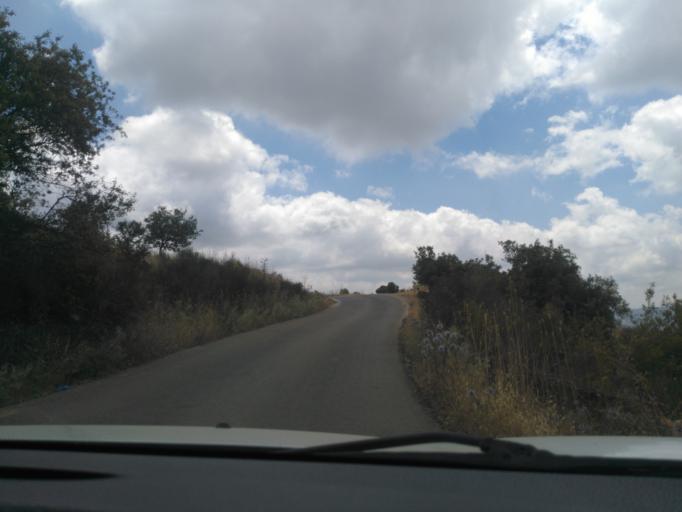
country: LB
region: Mont-Liban
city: Beit ed Dine
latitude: 33.6814
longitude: 35.6642
